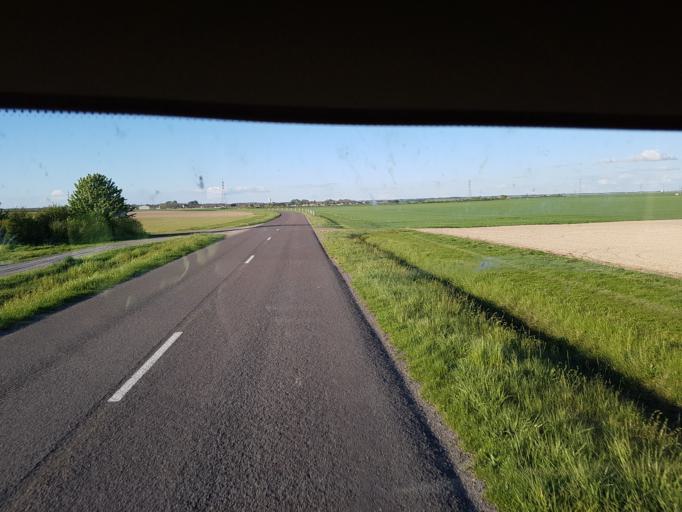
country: FR
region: Champagne-Ardenne
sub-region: Departement de l'Aube
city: Romilly-sur-Seine
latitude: 48.4699
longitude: 3.7203
